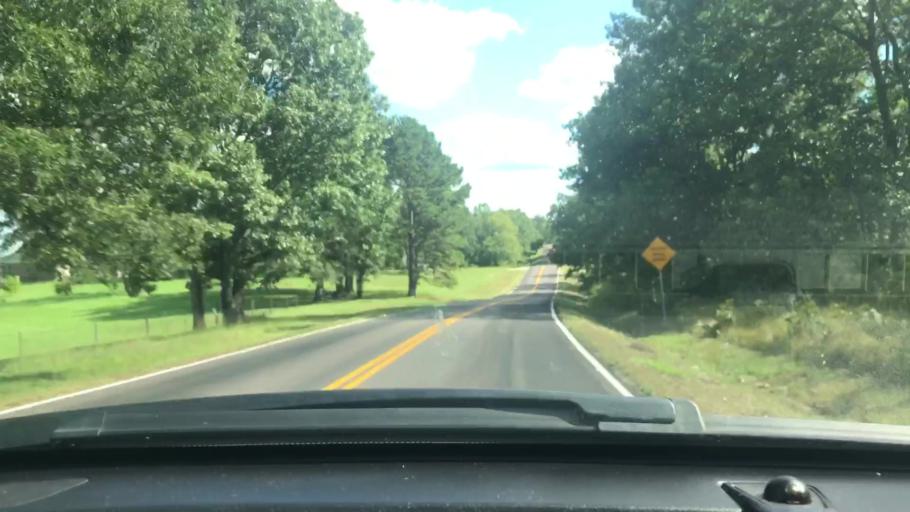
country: US
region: Missouri
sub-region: Wright County
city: Hartville
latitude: 37.3762
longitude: -92.3556
